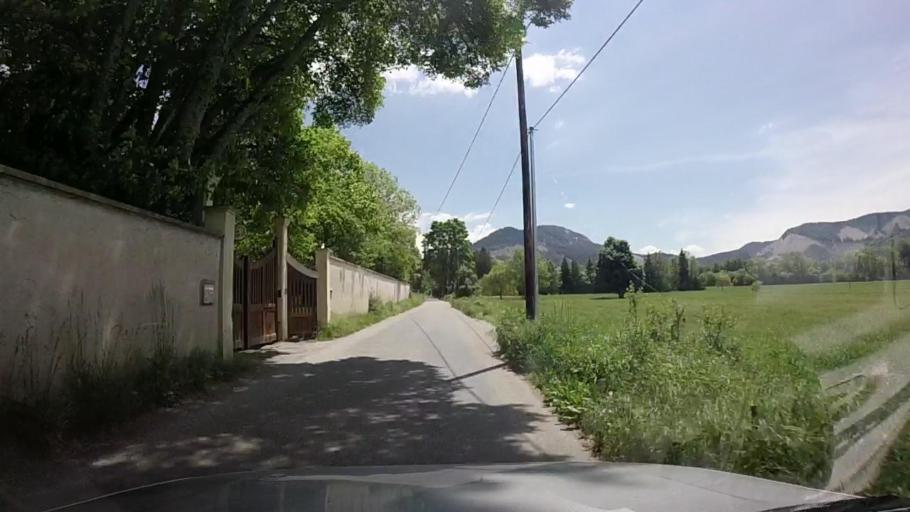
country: FR
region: Provence-Alpes-Cote d'Azur
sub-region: Departement des Alpes-de-Haute-Provence
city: Seyne-les-Alpes
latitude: 44.3494
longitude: 6.3513
